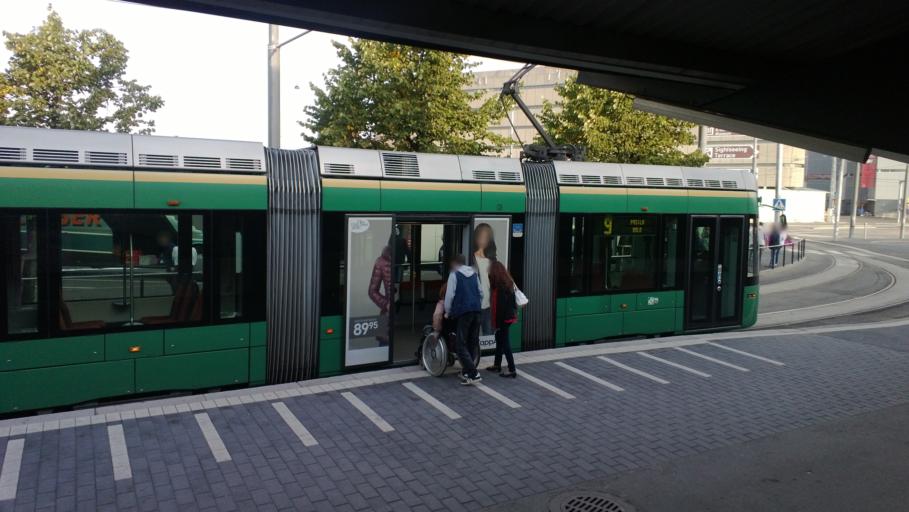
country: FI
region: Uusimaa
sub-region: Helsinki
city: Helsinki
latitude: 60.1545
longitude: 24.9206
